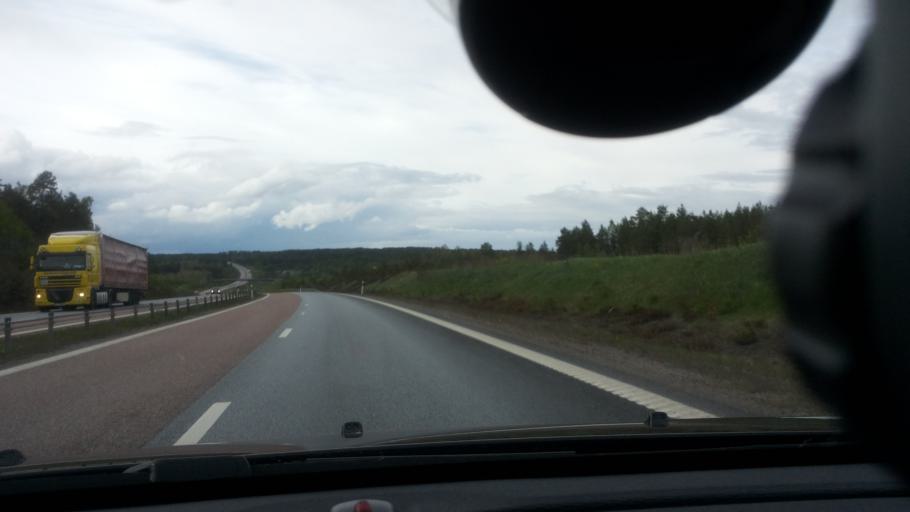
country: SE
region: Gaevleborg
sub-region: Soderhamns Kommun
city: Soderhamn
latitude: 61.3465
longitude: 17.0196
